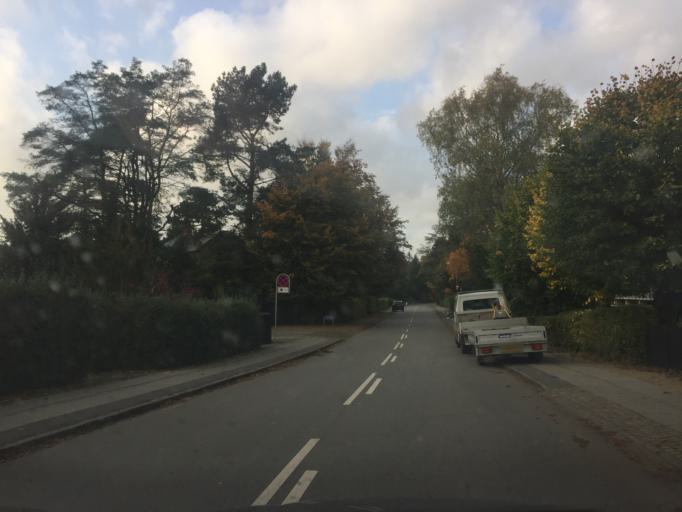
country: DK
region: Capital Region
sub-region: Herlev Kommune
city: Herlev
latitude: 55.7662
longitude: 12.4459
